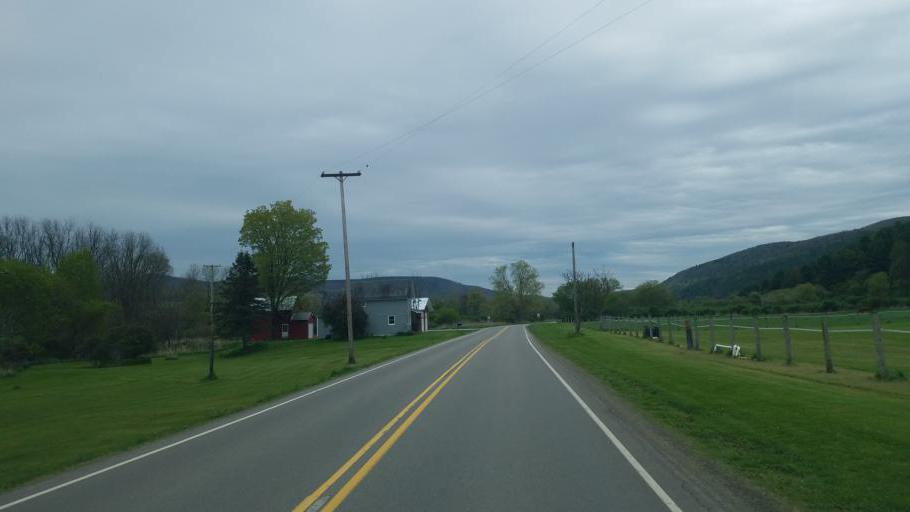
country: US
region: Pennsylvania
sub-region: Tioga County
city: Westfield
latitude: 41.9921
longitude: -77.4923
